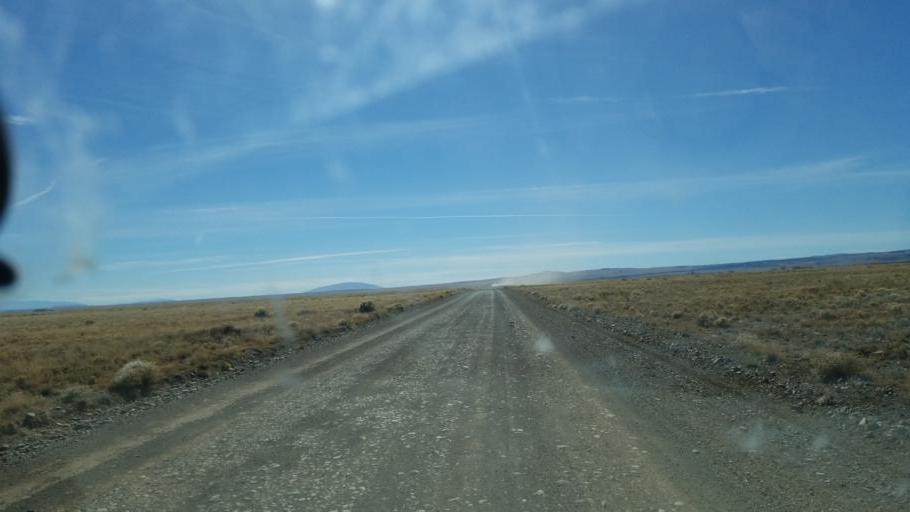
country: US
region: Colorado
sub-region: Rio Grande County
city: Monte Vista
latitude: 37.3378
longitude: -106.1490
